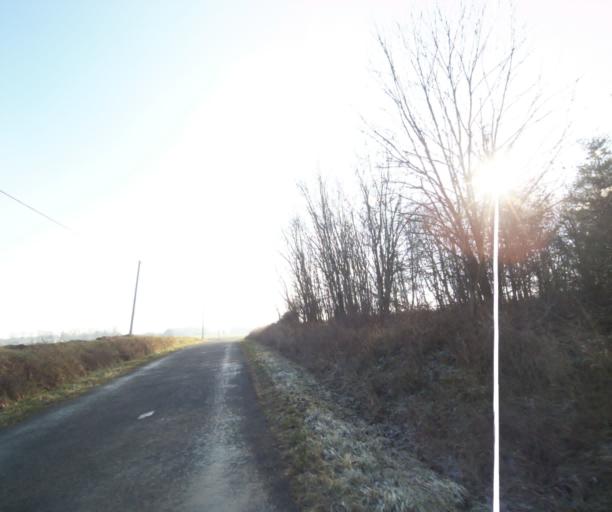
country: FR
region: Champagne-Ardenne
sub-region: Departement de la Haute-Marne
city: Bienville
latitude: 48.4974
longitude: 5.0575
